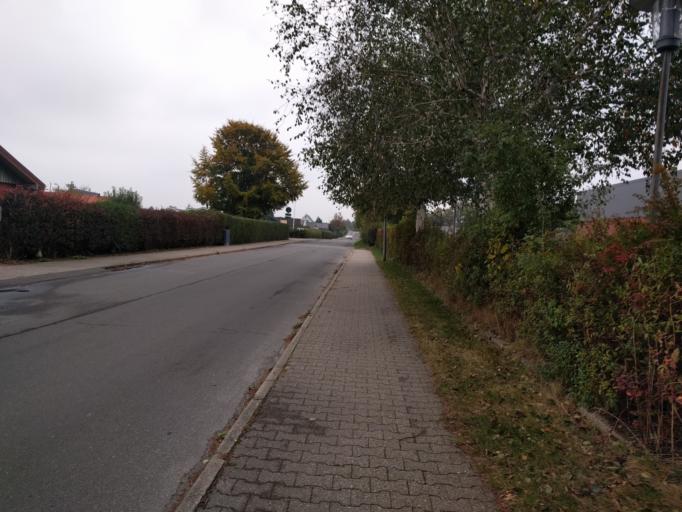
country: DK
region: South Denmark
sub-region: Fredericia Kommune
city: Snoghoj
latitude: 55.5412
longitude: 9.7106
